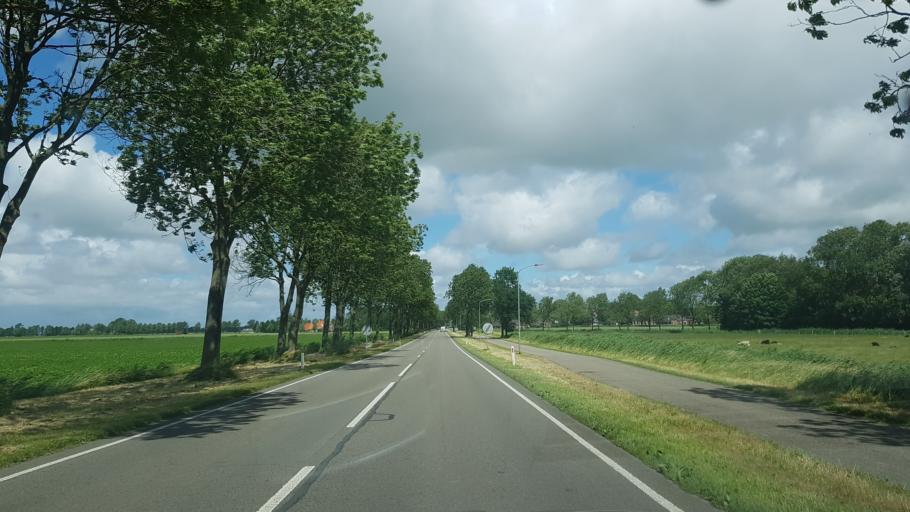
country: NL
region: Groningen
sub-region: Gemeente Winsum
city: Winsum
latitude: 53.3647
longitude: 6.5116
